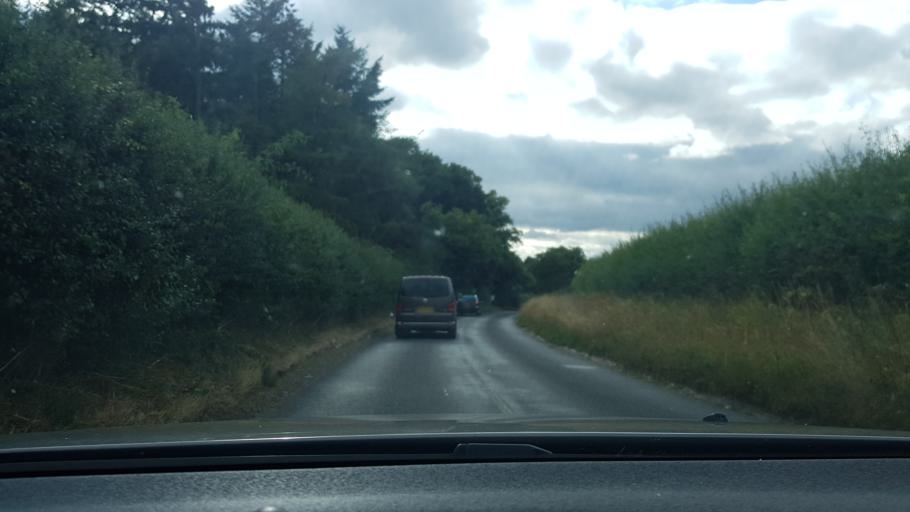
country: GB
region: England
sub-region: West Berkshire
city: Hermitage
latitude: 51.4655
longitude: -1.2127
